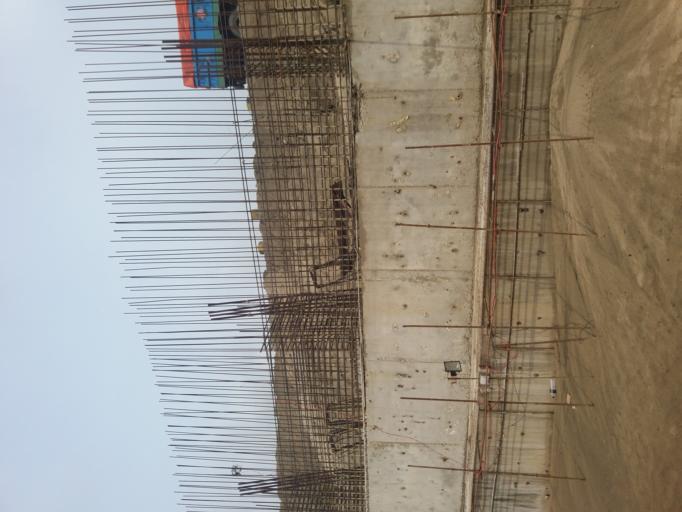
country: BD
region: Chittagong
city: Feni
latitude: 23.0414
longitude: 91.3657
